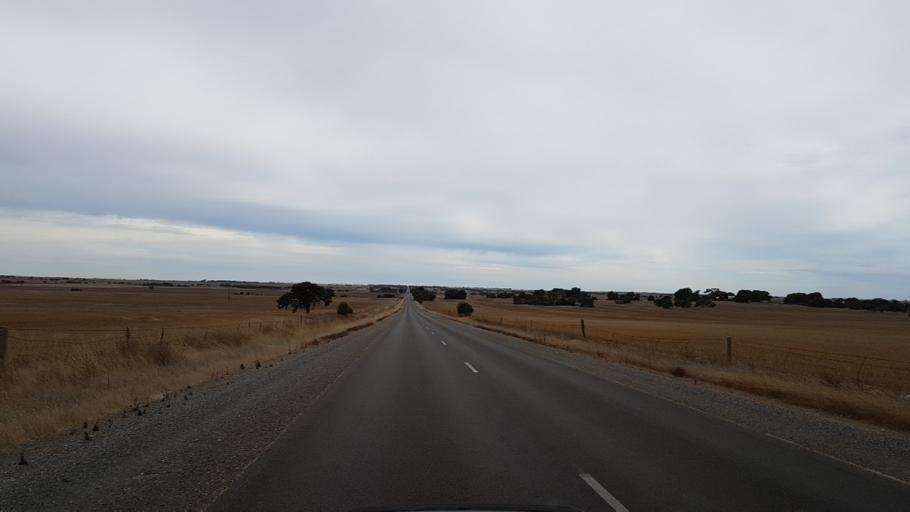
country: AU
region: South Australia
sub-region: Yorke Peninsula
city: Honiton
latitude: -34.9849
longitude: 137.3157
